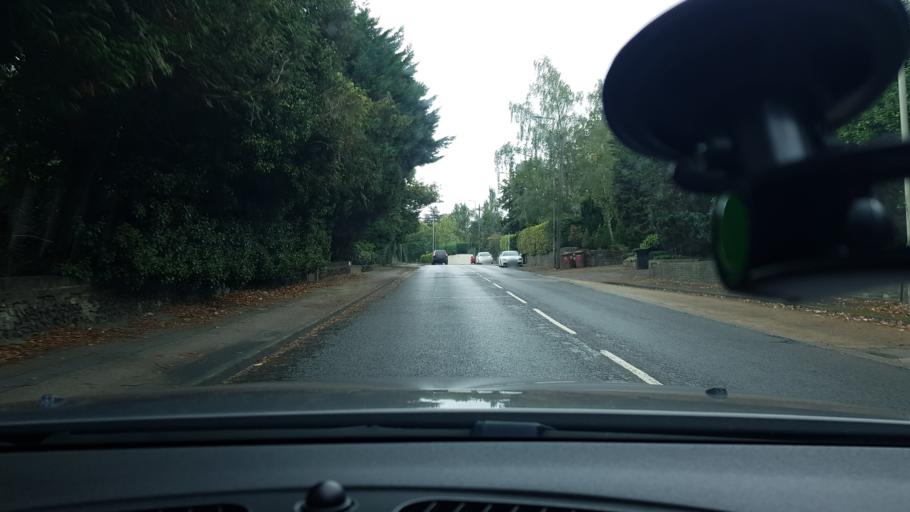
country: GB
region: England
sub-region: Hertfordshire
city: Chorleywood
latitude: 51.6513
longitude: -0.4823
